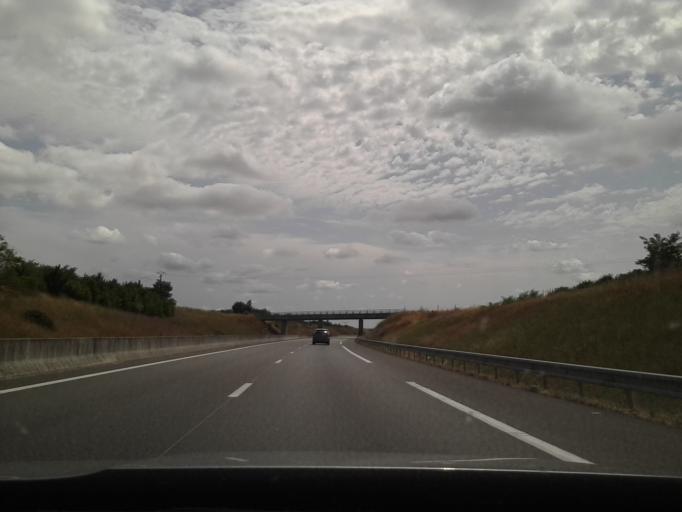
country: FR
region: Centre
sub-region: Departement d'Indre-et-Loire
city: Parcay-Meslay
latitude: 47.4810
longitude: 0.7476
